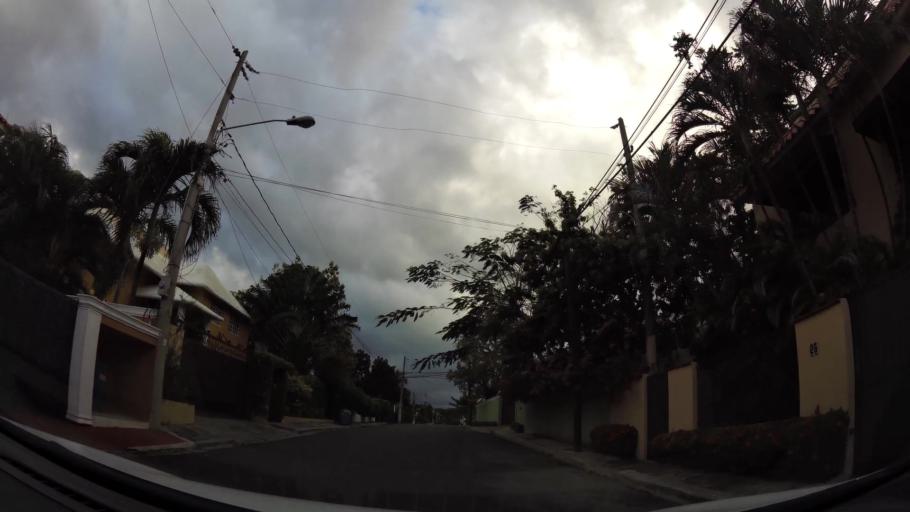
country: DO
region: Nacional
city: Santo Domingo
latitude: 18.5011
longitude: -69.9719
